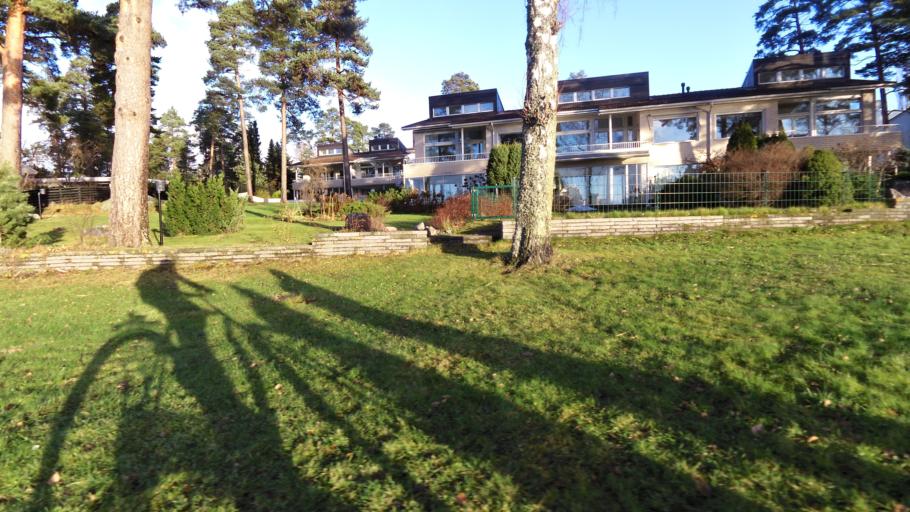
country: FI
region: Uusimaa
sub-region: Helsinki
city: Koukkuniemi
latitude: 60.1443
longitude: 24.7472
